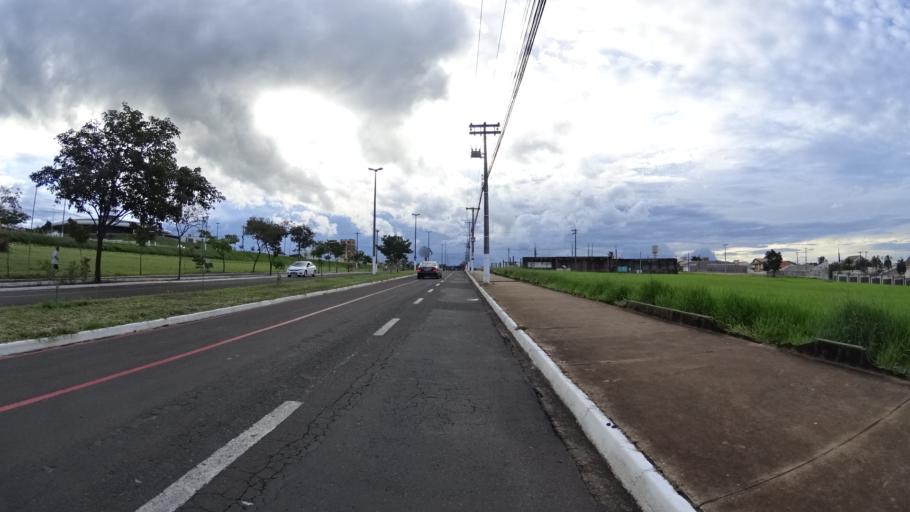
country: BR
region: Sao Paulo
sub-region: Marilia
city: Marilia
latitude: -22.2287
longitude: -49.9206
